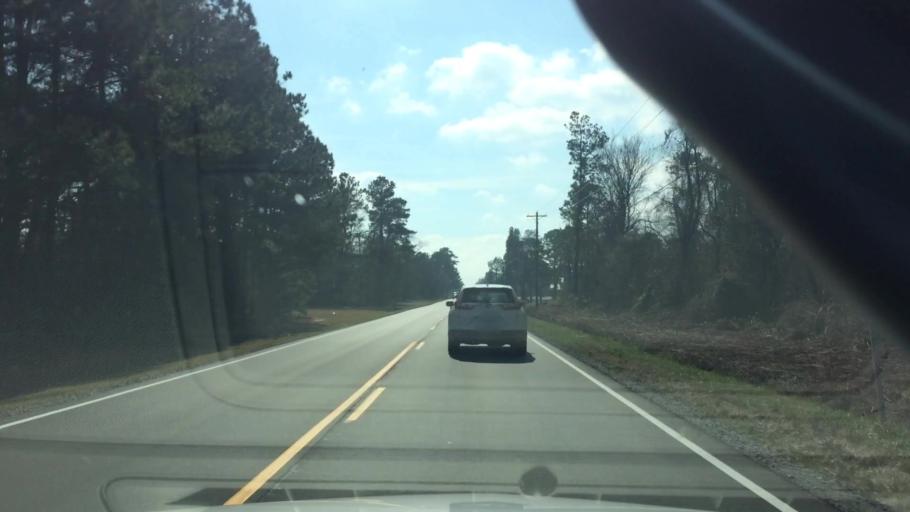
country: US
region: North Carolina
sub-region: Duplin County
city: Beulaville
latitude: 34.9782
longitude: -77.7604
